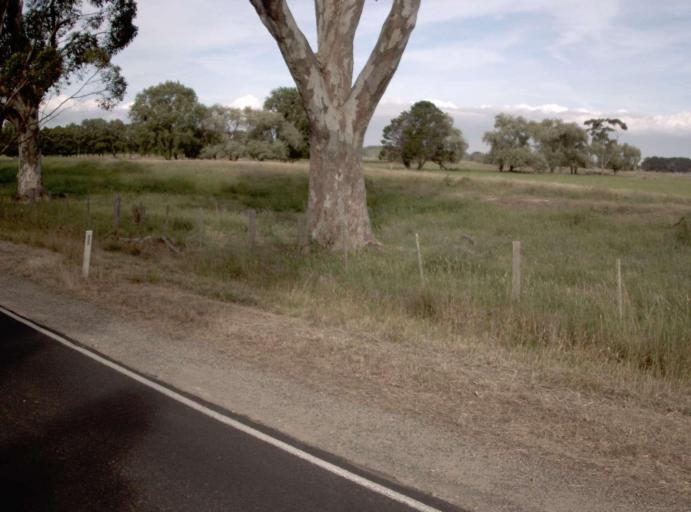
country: AU
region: Victoria
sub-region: Wellington
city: Heyfield
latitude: -38.0152
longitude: 146.7727
